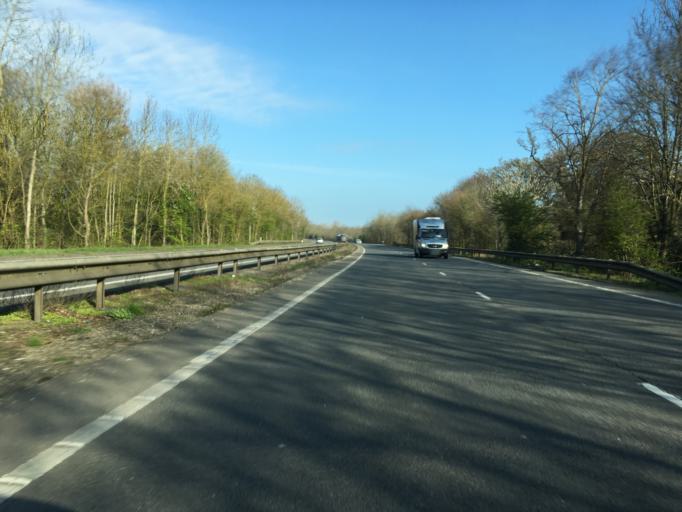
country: GB
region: England
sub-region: Milton Keynes
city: Stony Stratford
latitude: 52.0579
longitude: -0.8396
